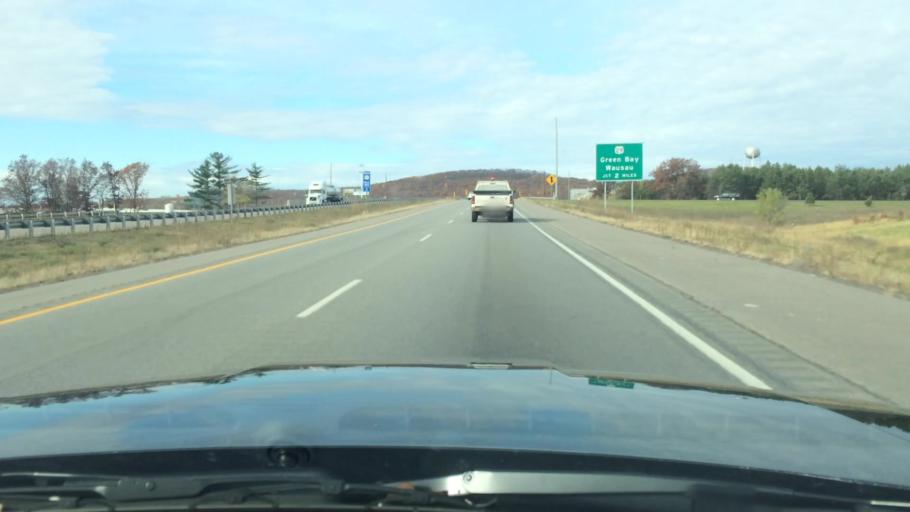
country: US
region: Wisconsin
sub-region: Marathon County
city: Evergreen
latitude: 44.8612
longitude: -89.6392
